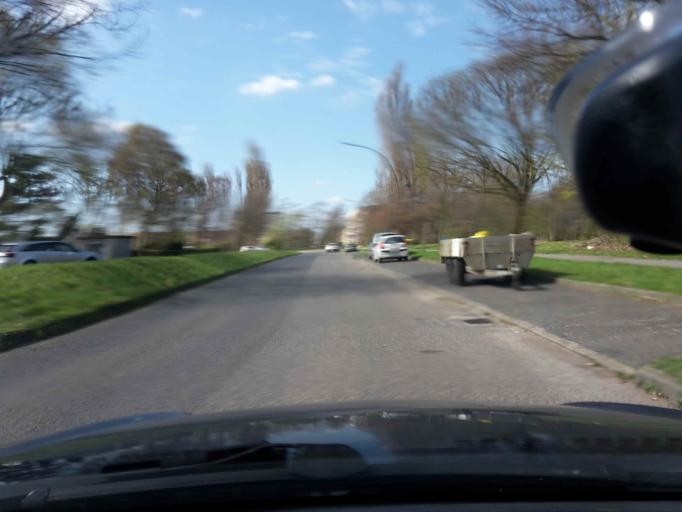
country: DE
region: Hamburg
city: Rothenburgsort
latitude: 53.5466
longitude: 10.0632
